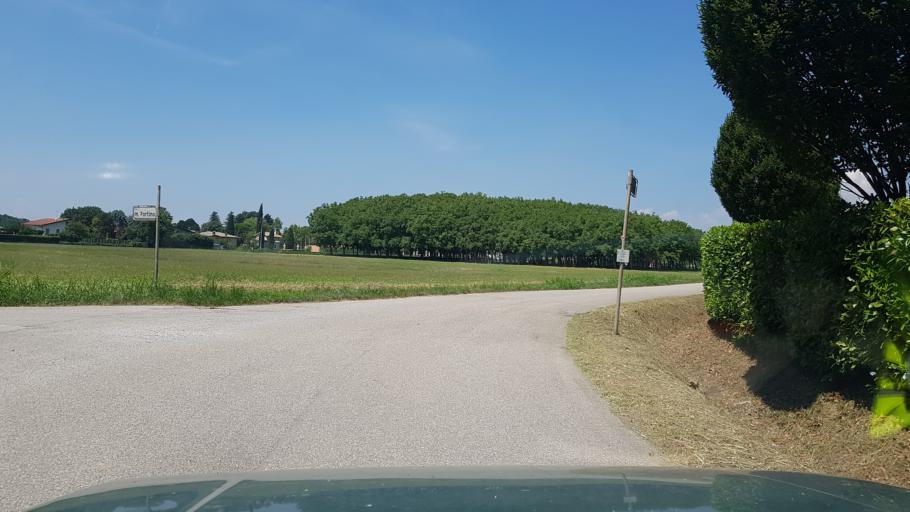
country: IT
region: Friuli Venezia Giulia
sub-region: Provincia di Gorizia
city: Farra d'Isonzo
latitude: 45.9111
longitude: 13.5368
